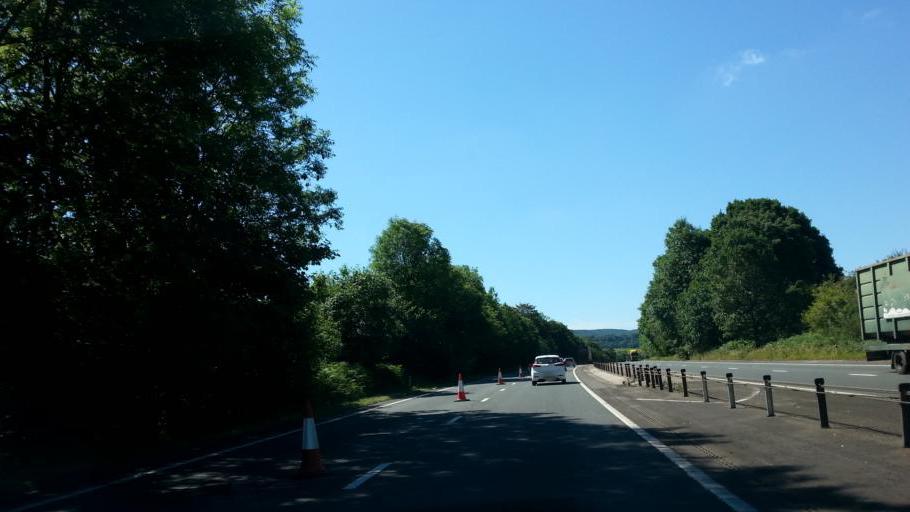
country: GB
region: Wales
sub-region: Monmouthshire
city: Llanbadoc
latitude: 51.6805
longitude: -2.8760
